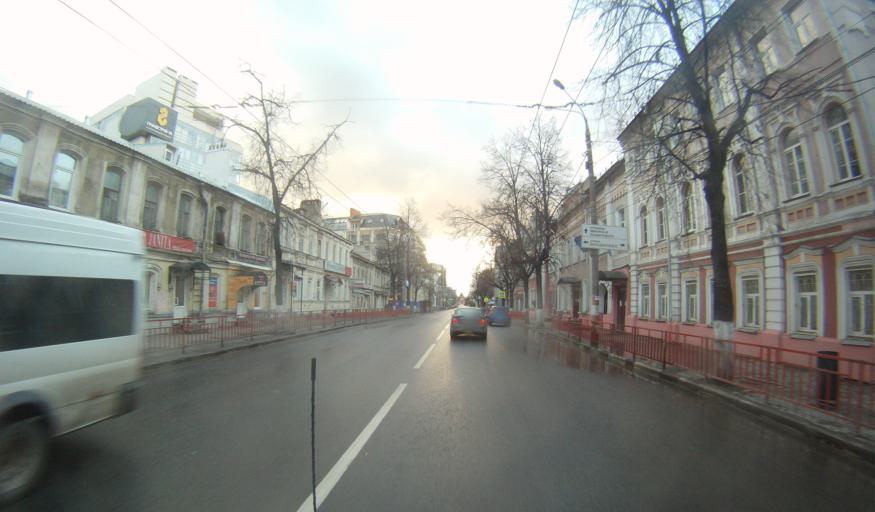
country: RU
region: Nizjnij Novgorod
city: Nizhniy Novgorod
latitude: 56.3184
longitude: 44.0142
